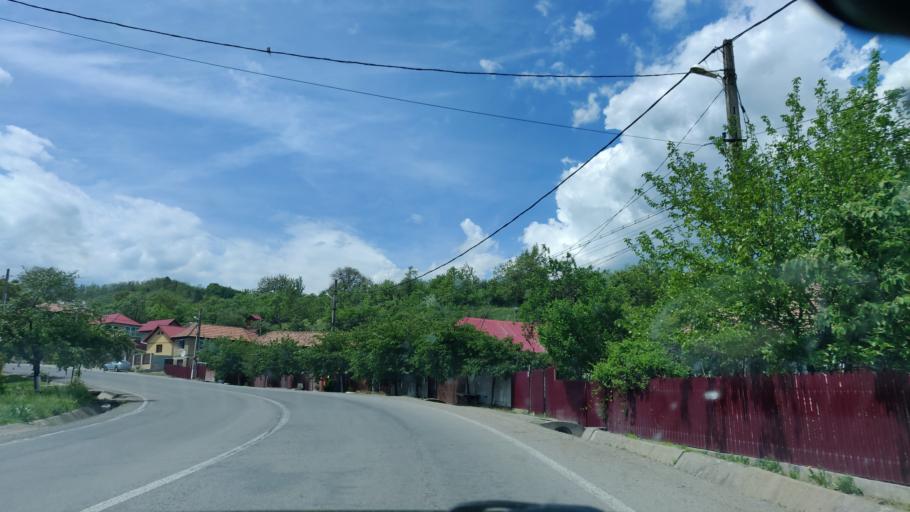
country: RO
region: Vrancea
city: Matacina
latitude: 45.8917
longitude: 26.8399
